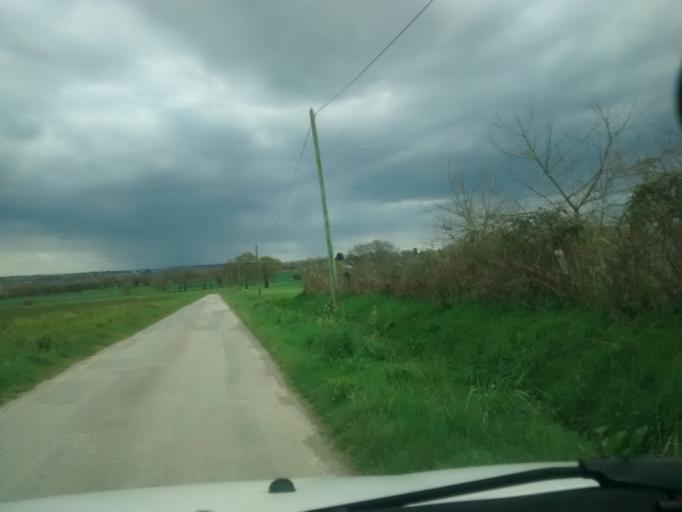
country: FR
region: Brittany
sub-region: Departement d'Ille-et-Vilaine
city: Servon-sur-Vilaine
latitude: 48.1517
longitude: -1.4912
